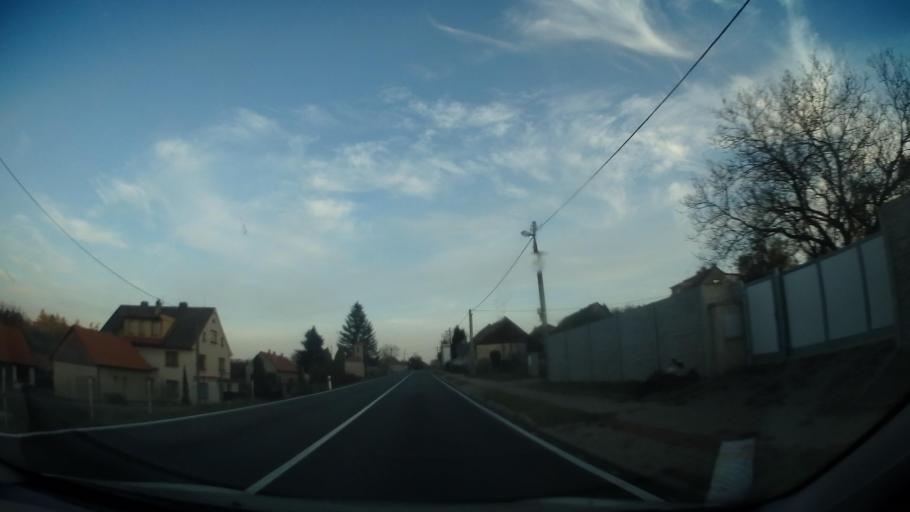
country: CZ
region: Central Bohemia
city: Vlasim
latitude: 49.6874
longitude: 14.9347
